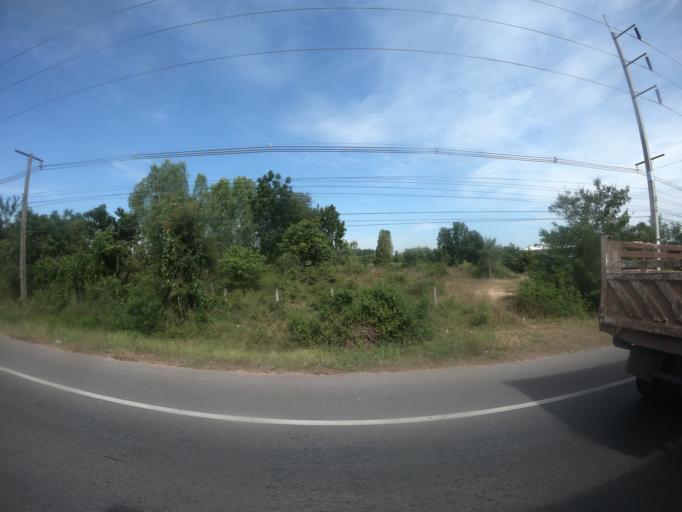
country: TH
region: Maha Sarakham
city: Chiang Yuen
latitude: 16.4452
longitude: 103.0216
